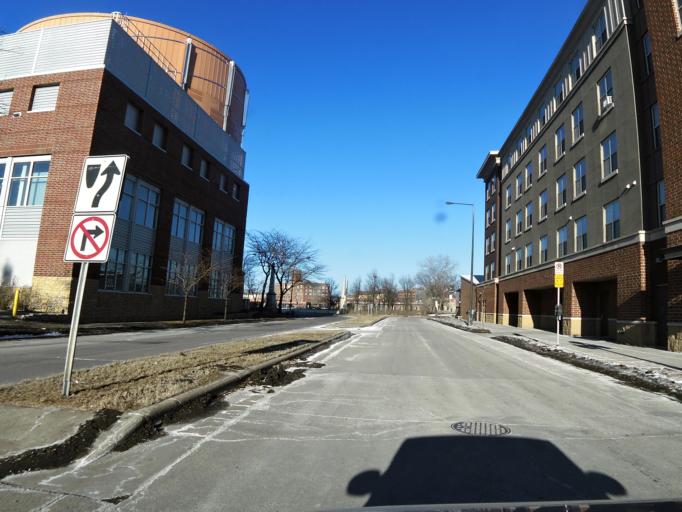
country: US
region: Minnesota
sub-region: Ramsey County
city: Saint Paul
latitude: 44.9528
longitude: -93.0916
